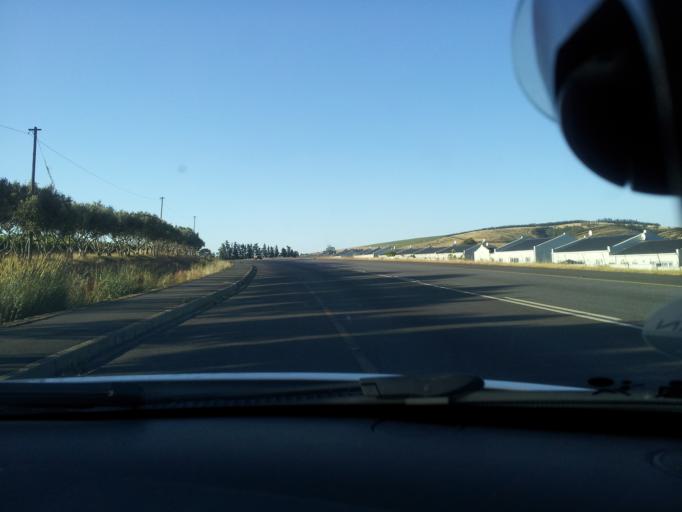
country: ZA
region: Western Cape
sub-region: Cape Winelands District Municipality
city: Stellenbosch
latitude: -33.9100
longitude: 18.8473
